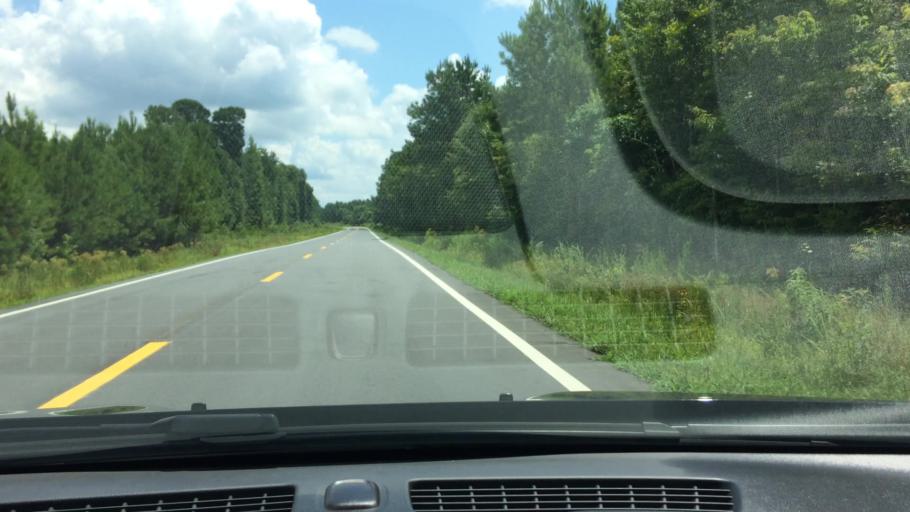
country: US
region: North Carolina
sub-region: Craven County
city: Vanceboro
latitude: 35.4290
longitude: -77.1840
